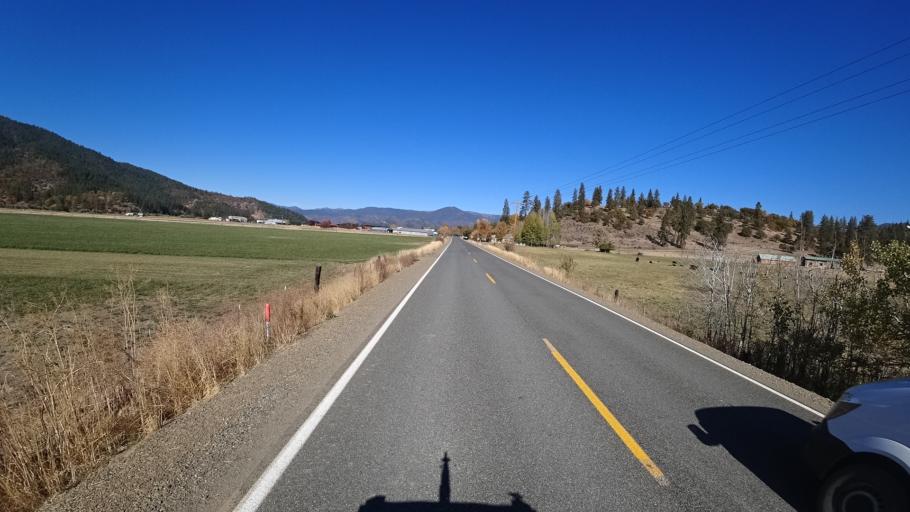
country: US
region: California
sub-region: Siskiyou County
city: Yreka
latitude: 41.5978
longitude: -122.8438
